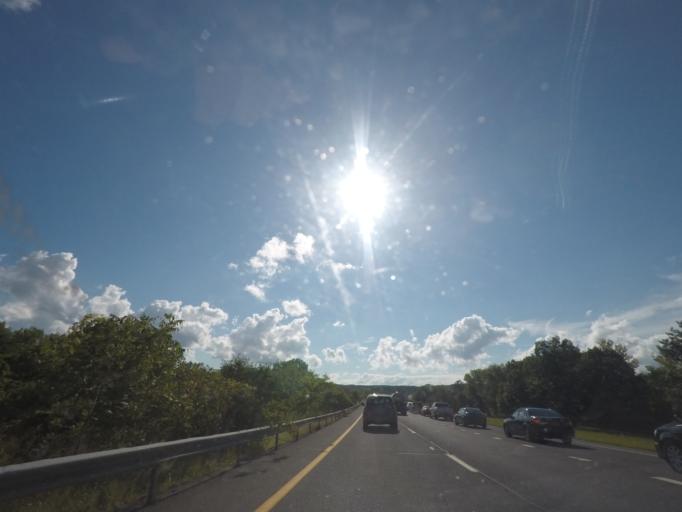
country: US
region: New York
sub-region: Albany County
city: Menands
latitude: 42.6997
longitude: -73.7122
